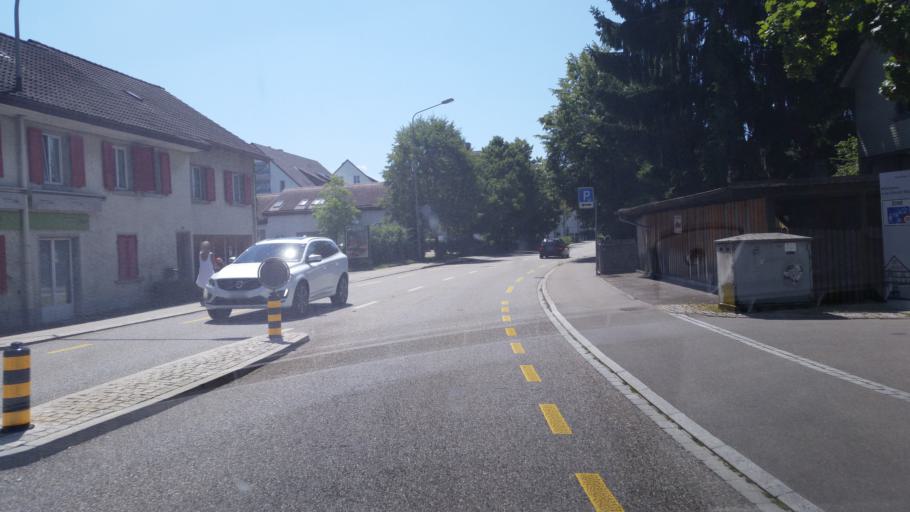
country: CH
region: Zurich
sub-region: Bezirk Buelach
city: Buelach / Seematt
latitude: 47.5180
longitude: 8.5425
